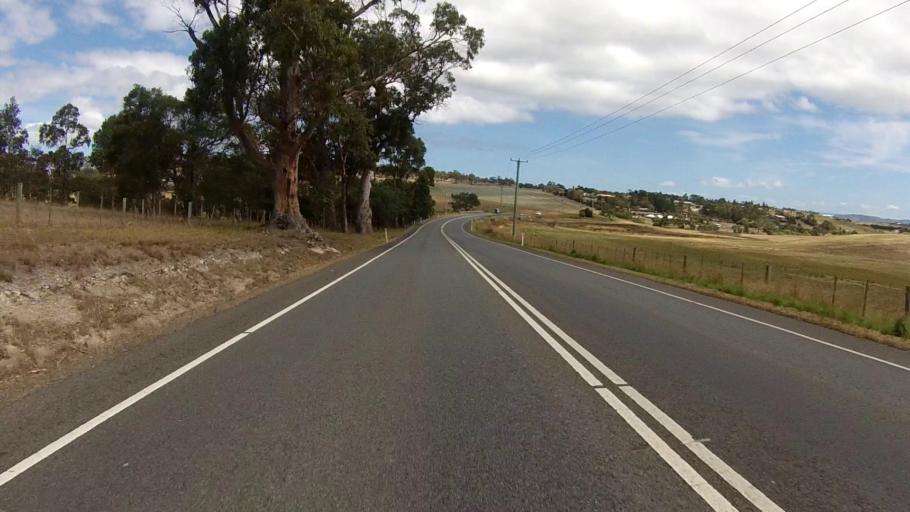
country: AU
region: Tasmania
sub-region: Sorell
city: Sorell
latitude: -42.8080
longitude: 147.6287
